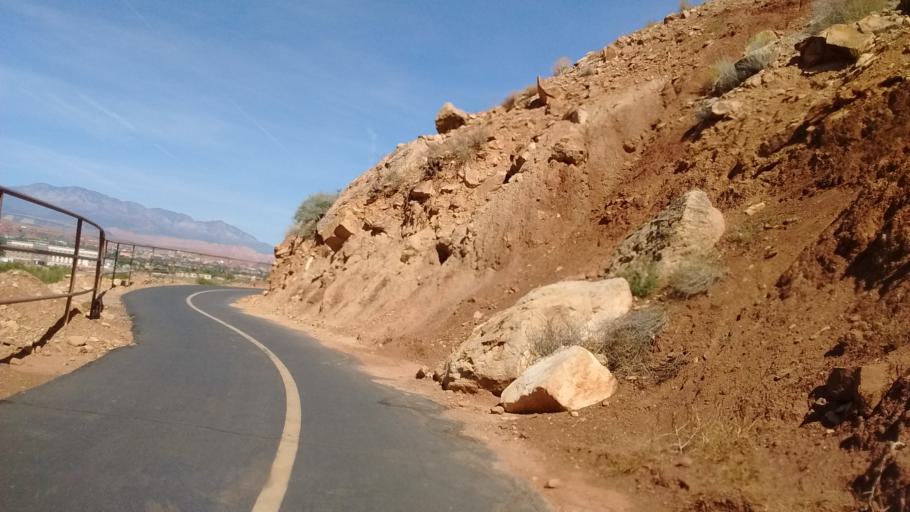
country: US
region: Utah
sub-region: Washington County
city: Saint George
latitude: 37.0699
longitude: -113.5819
